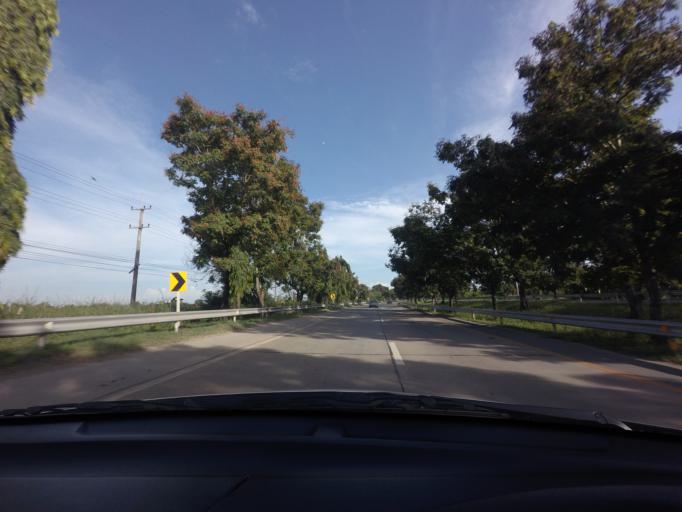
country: TH
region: Phra Nakhon Si Ayutthaya
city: Lat Bua Luang
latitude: 14.1992
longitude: 100.2926
